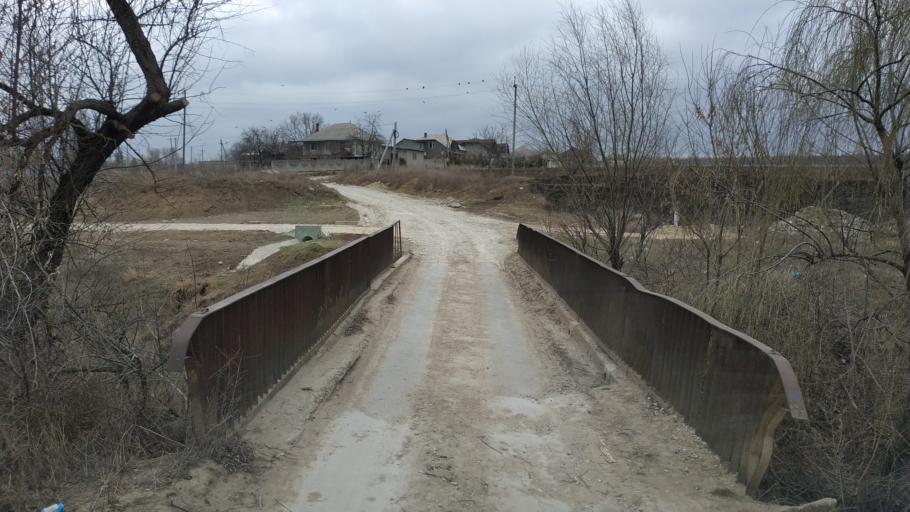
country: MD
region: Laloveni
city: Ialoveni
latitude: 46.9323
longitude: 28.7948
